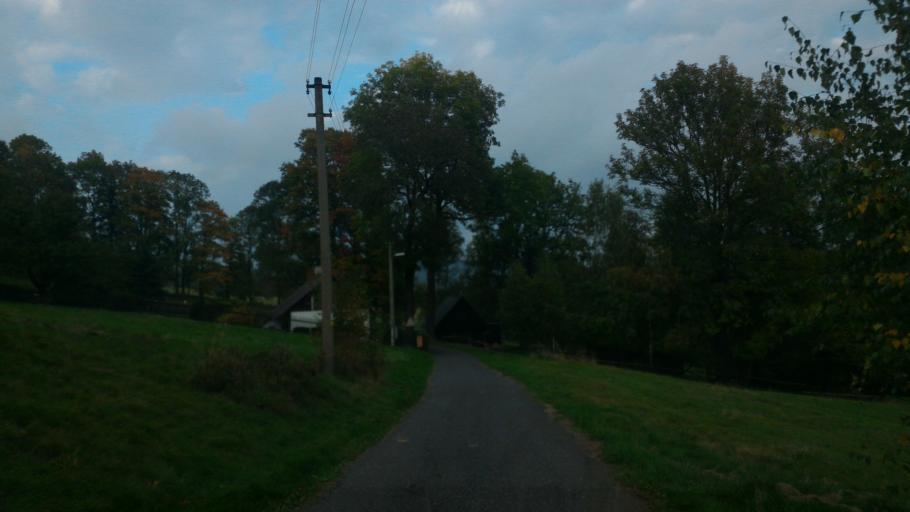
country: CZ
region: Ustecky
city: Dolni Podluzi
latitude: 50.8645
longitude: 14.5734
